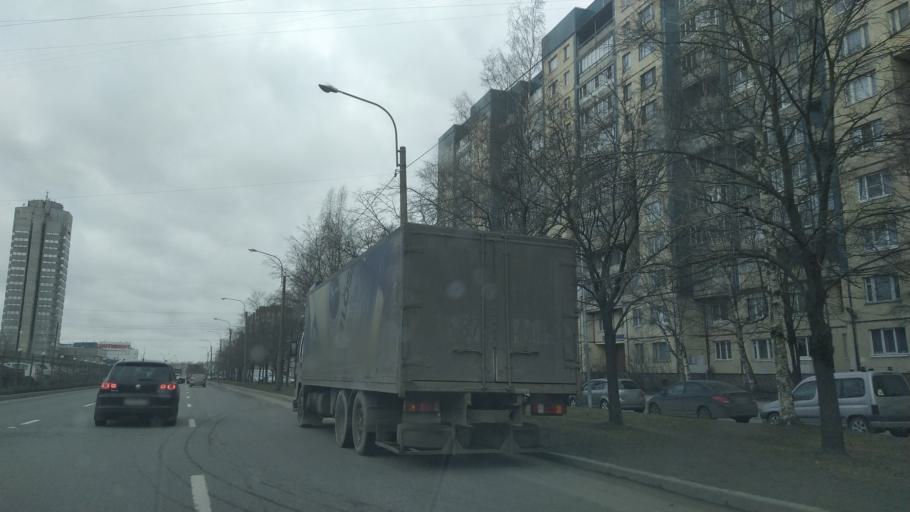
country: RU
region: St.-Petersburg
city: Komendantsky aerodrom
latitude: 60.0091
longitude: 30.2741
